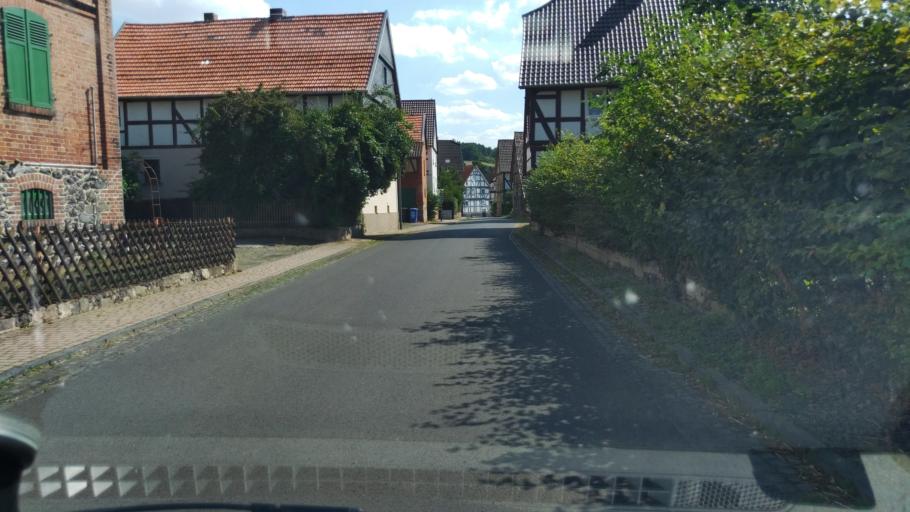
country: DE
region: Hesse
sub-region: Regierungsbezirk Kassel
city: Wabern
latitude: 51.1029
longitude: 9.3868
